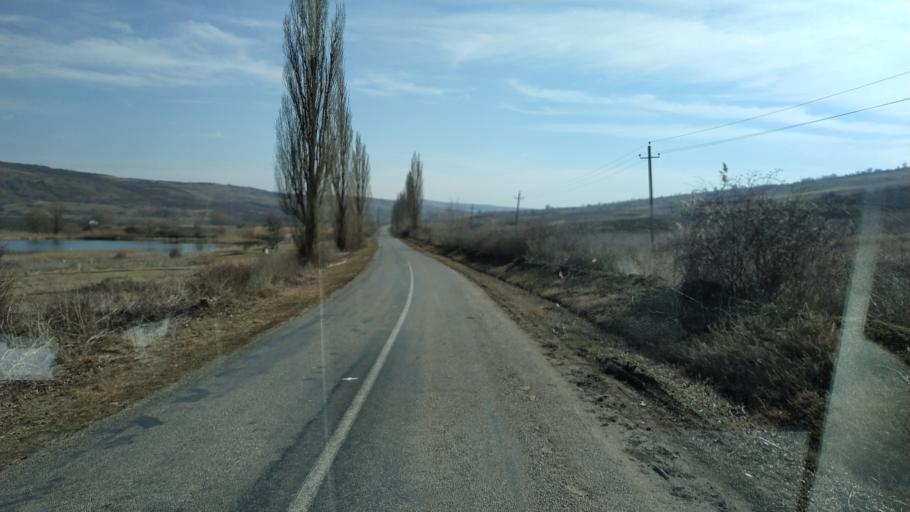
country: MD
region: Nisporeni
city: Nisporeni
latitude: 47.1723
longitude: 28.0896
